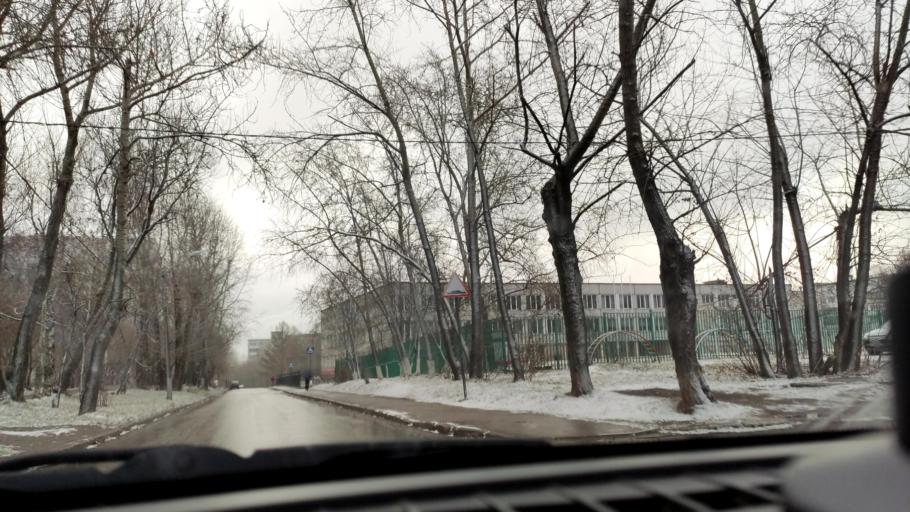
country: RU
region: Perm
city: Perm
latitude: 57.9833
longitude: 56.2193
